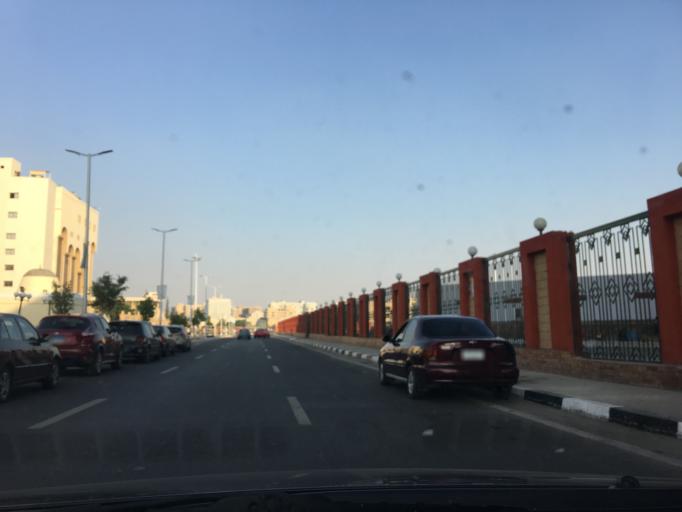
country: EG
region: Muhafazat al Qahirah
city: Cairo
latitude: 30.0728
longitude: 31.3081
